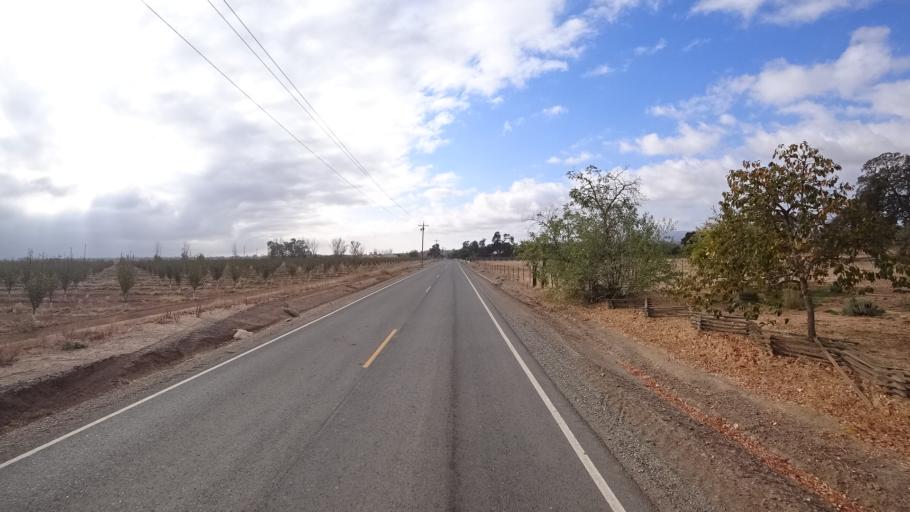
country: US
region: California
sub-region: Yolo County
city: Esparto
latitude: 38.7197
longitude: -122.0469
